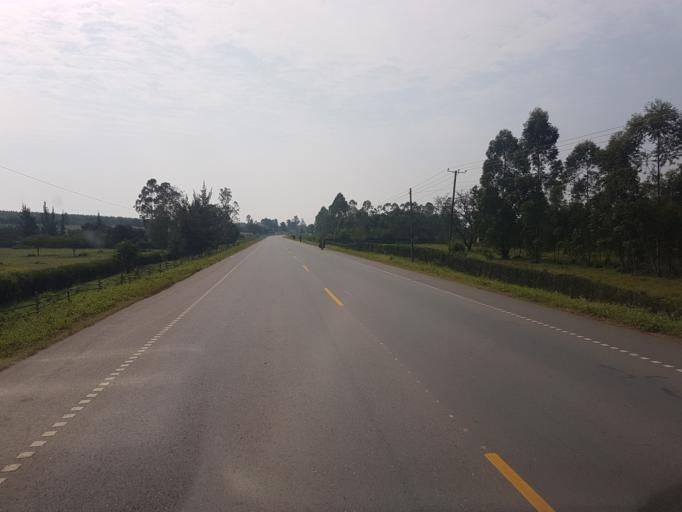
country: UG
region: Western Region
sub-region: Sheema District
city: Kibingo
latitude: -0.6348
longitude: 30.5326
